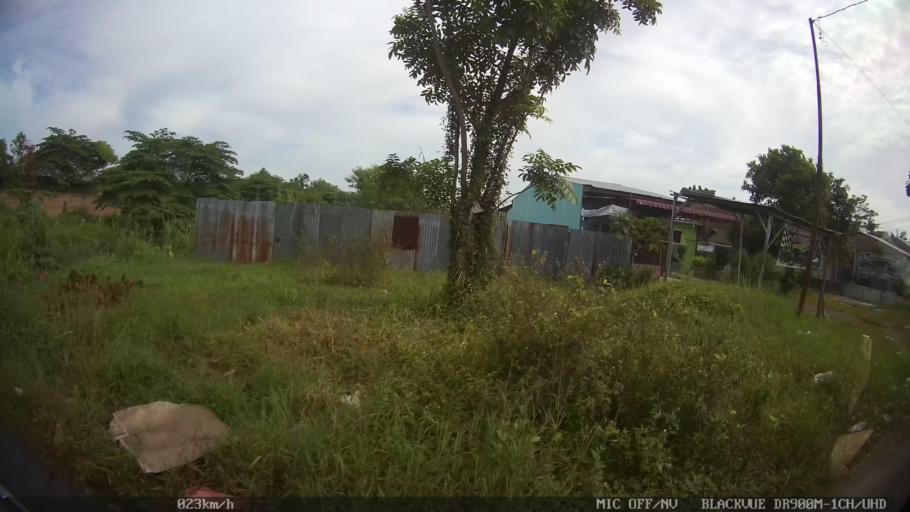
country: ID
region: North Sumatra
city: Medan
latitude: 3.6202
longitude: 98.7580
